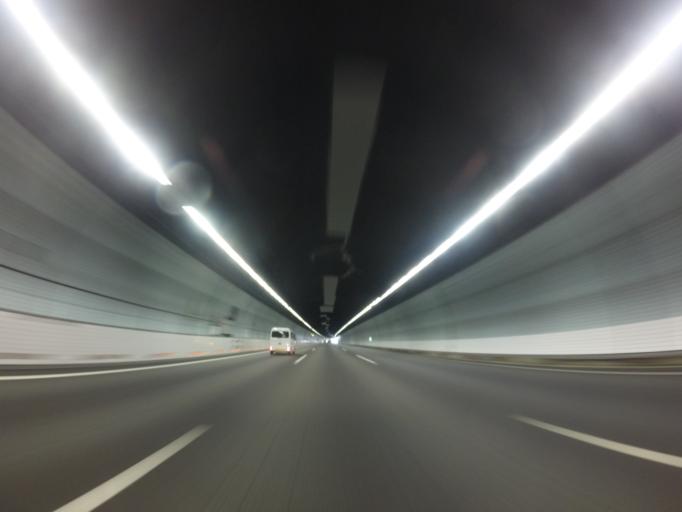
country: JP
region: Shizuoka
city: Yaizu
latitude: 34.9024
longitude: 138.3374
